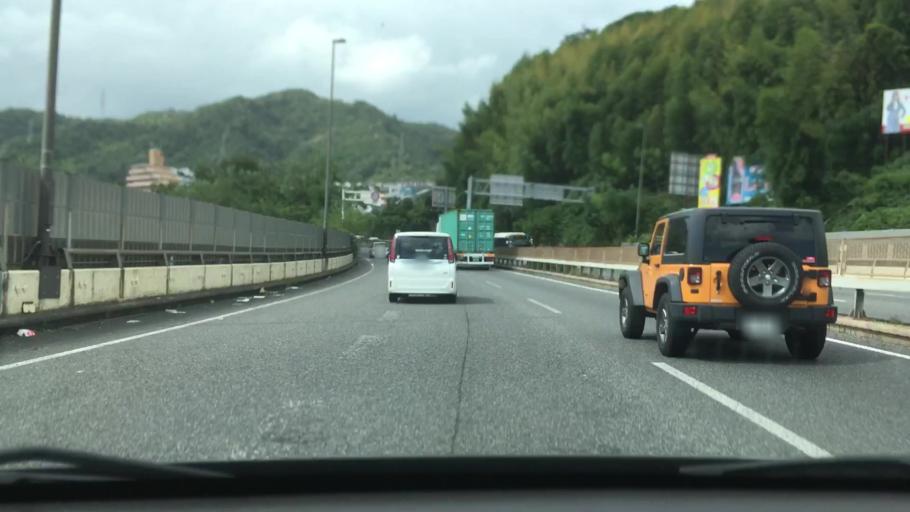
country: JP
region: Hiroshima
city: Hiroshima-shi
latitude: 34.3939
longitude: 132.4203
